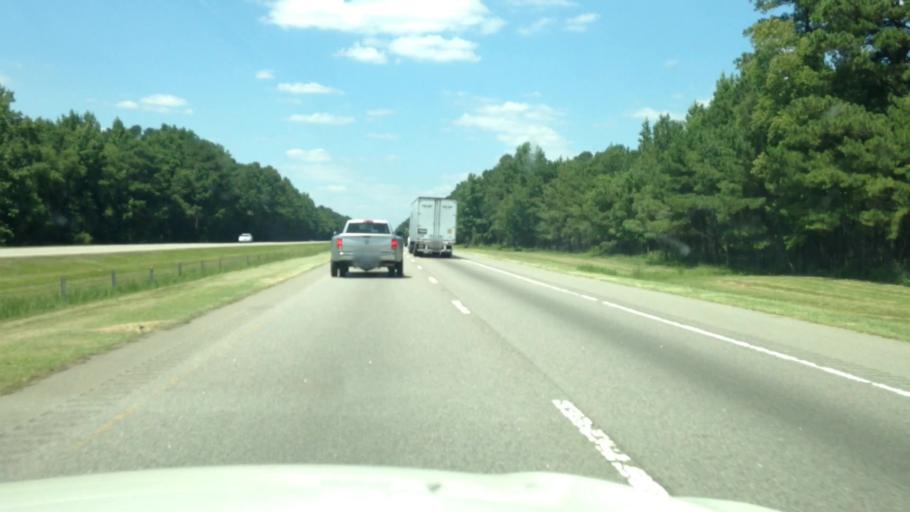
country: US
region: North Carolina
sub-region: Robeson County
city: Saint Pauls
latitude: 34.7712
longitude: -78.9960
